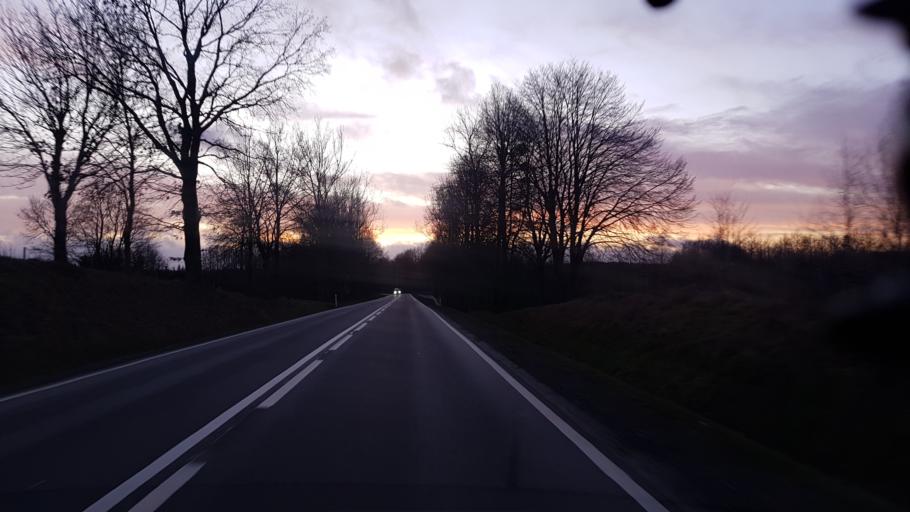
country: PL
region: Pomeranian Voivodeship
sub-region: Powiat bytowski
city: Tuchomie
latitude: 54.1310
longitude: 17.3899
